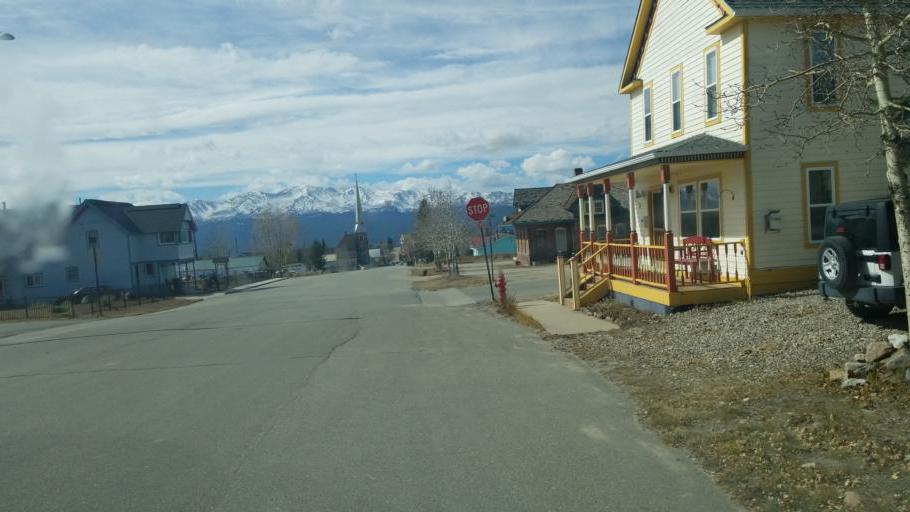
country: US
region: Colorado
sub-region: Lake County
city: Leadville
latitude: 39.2508
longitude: -106.2867
